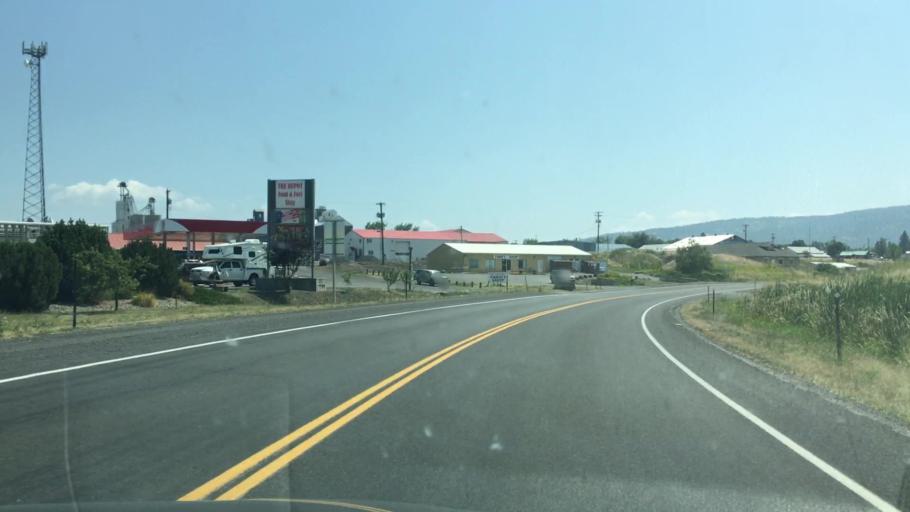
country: US
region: Idaho
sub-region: Idaho County
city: Grangeville
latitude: 45.9355
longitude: -116.1344
